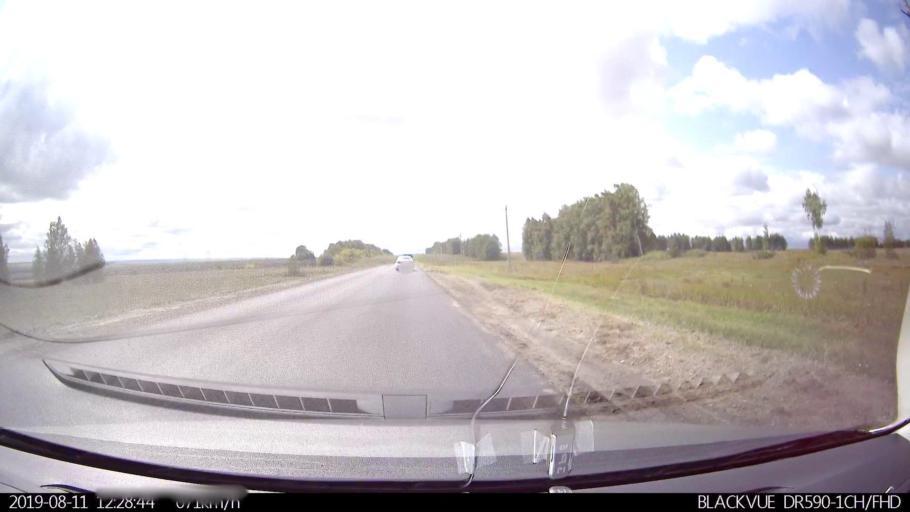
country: RU
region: Ulyanovsk
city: Ignatovka
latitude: 53.8408
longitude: 47.9091
